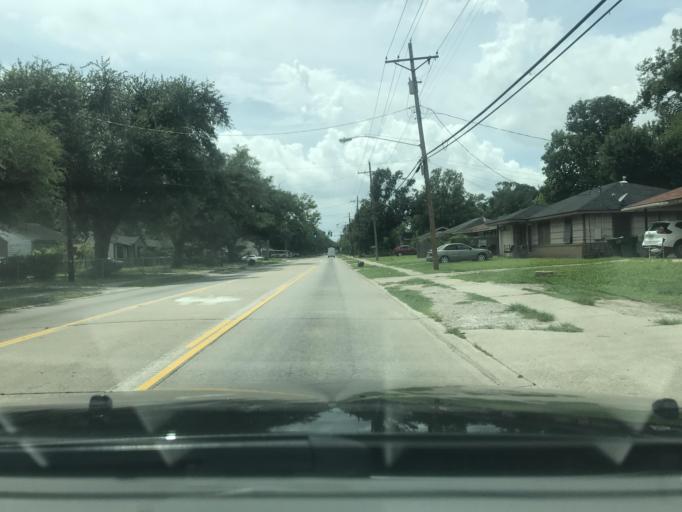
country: US
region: Louisiana
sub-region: Calcasieu Parish
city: Lake Charles
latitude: 30.2131
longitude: -93.1918
